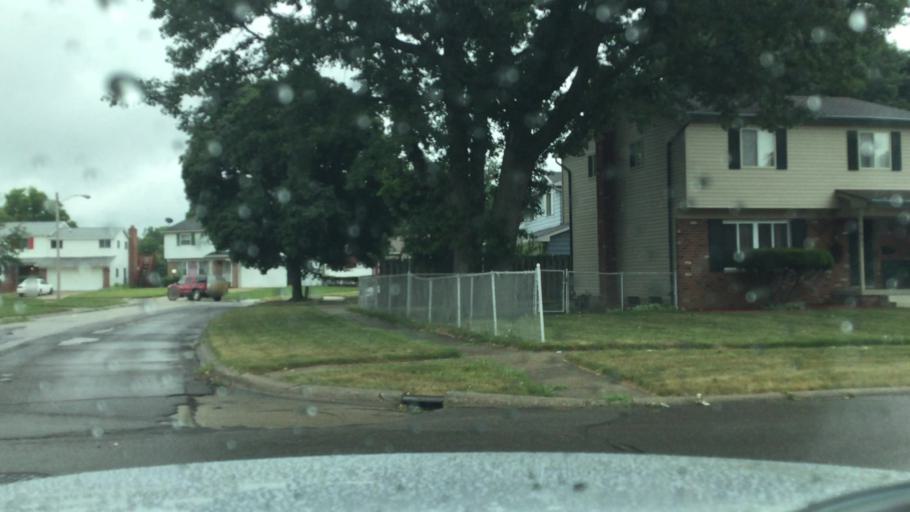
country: US
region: Michigan
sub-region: Genesee County
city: Beecher
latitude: 43.0707
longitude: -83.7226
